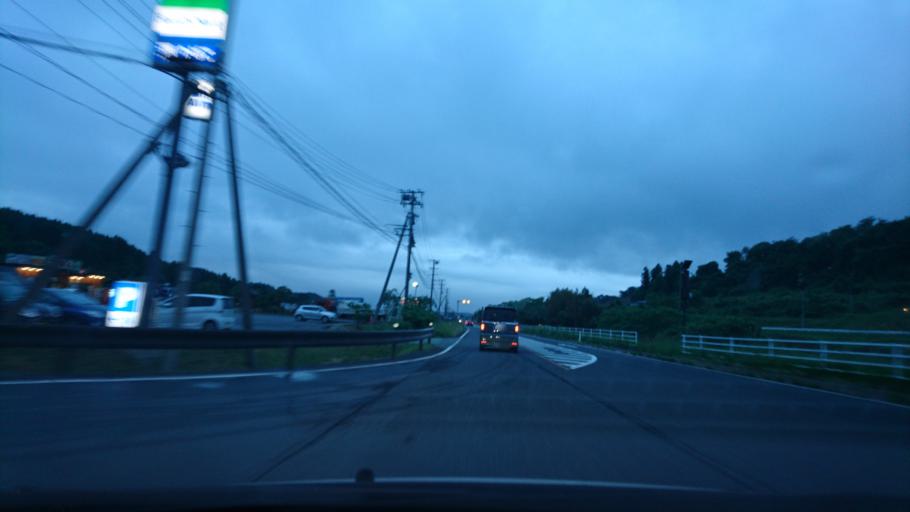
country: JP
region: Iwate
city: Ichinoseki
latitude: 38.8300
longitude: 141.0823
